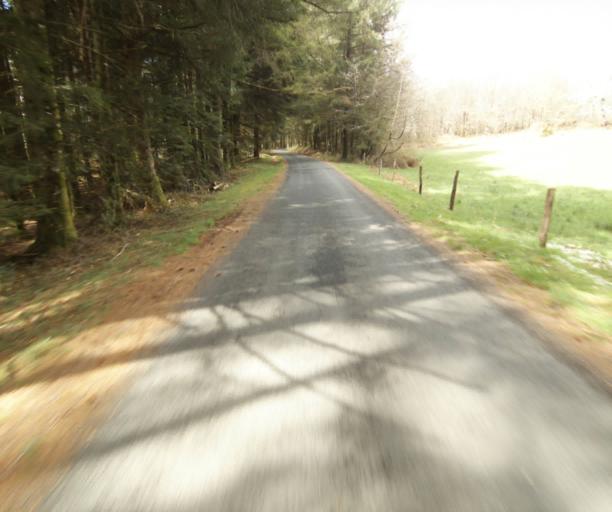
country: FR
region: Limousin
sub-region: Departement de la Correze
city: Argentat
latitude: 45.1951
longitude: 1.9100
